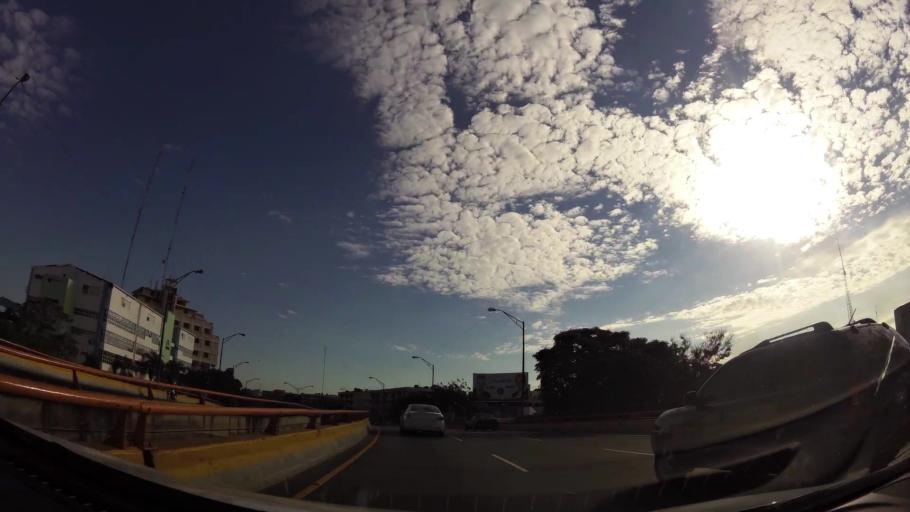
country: DO
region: Nacional
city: San Carlos
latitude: 18.4821
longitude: -69.9069
